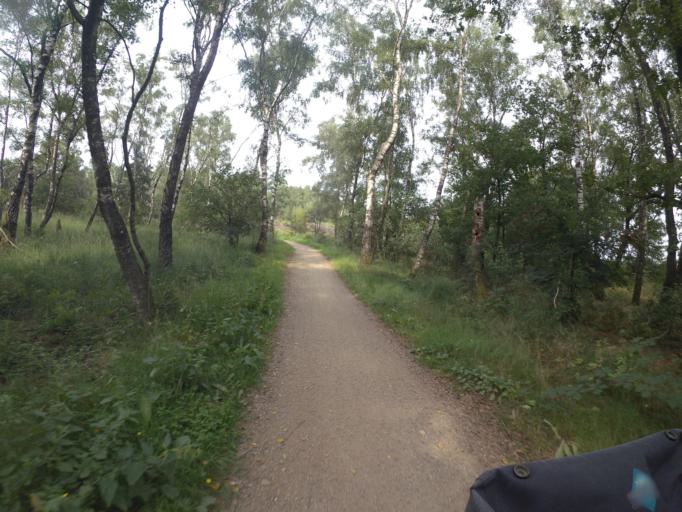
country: NL
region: Limburg
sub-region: Gemeente Bergen
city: Wellerlooi
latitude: 51.6100
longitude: 6.0739
